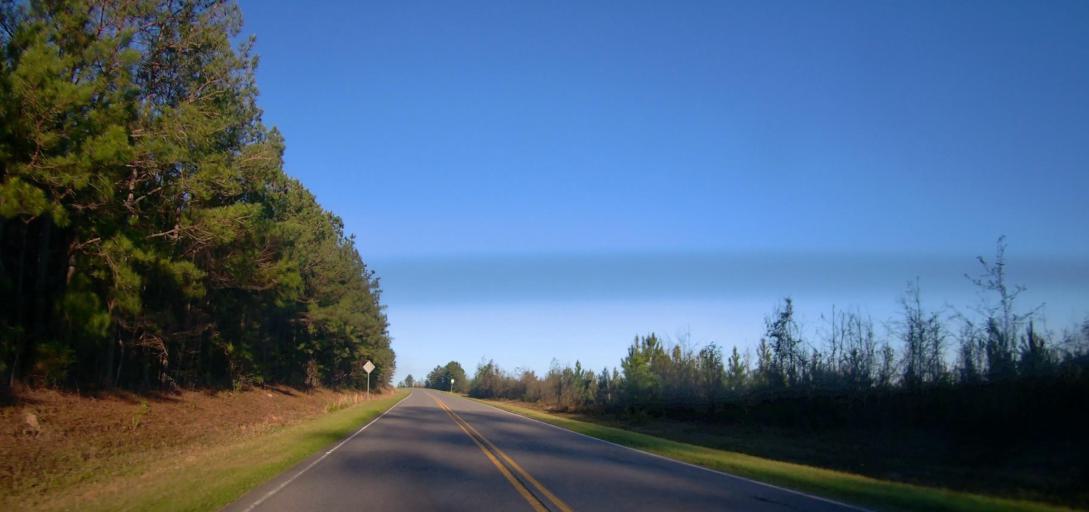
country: US
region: Georgia
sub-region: Wilkinson County
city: Gordon
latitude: 32.8779
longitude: -83.2699
